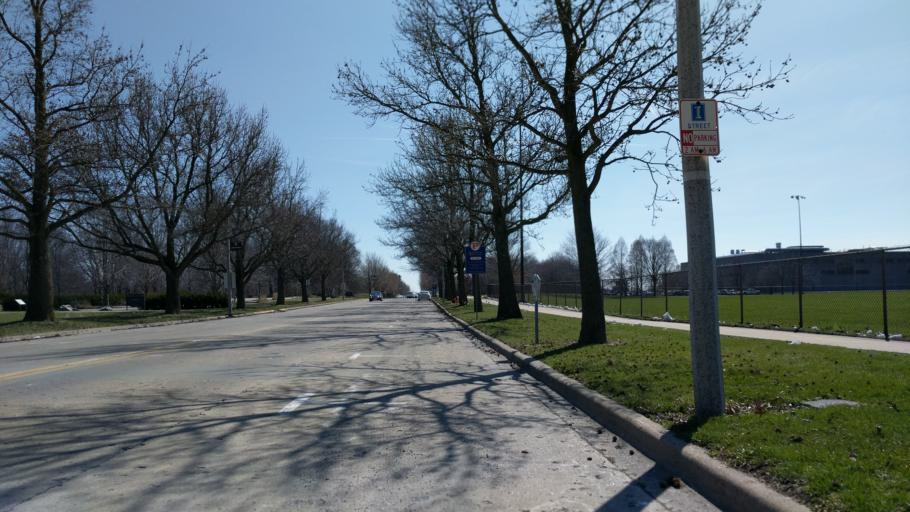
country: US
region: Illinois
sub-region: Champaign County
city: Urbana
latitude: 40.0959
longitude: -88.2191
